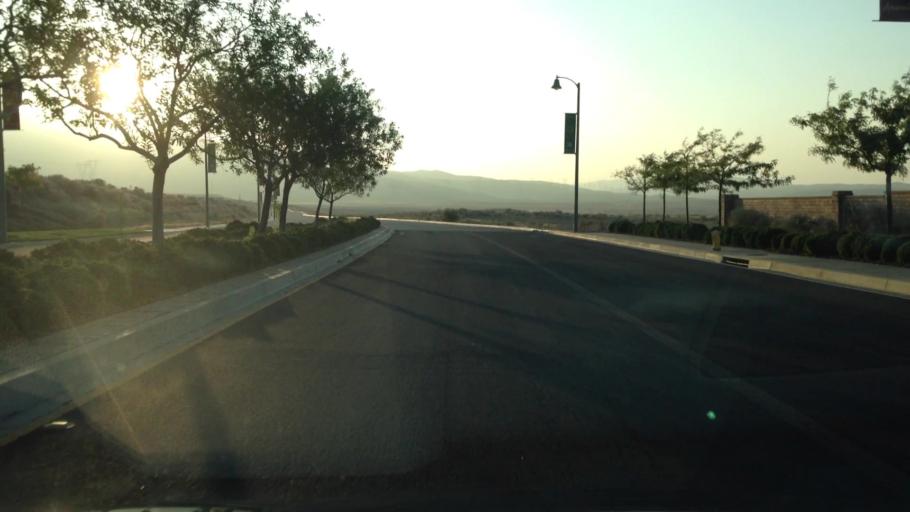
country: US
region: California
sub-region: Los Angeles County
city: Desert View Highlands
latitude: 34.5669
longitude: -118.1772
